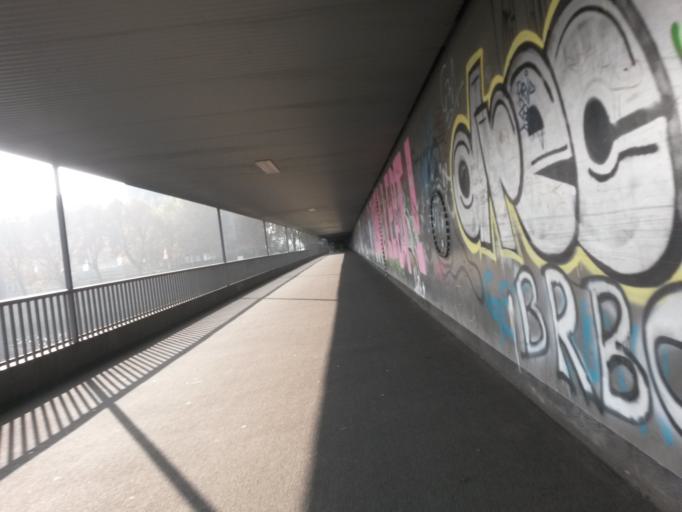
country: DE
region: Bremen
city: Bremen
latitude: 53.0801
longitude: 8.7908
